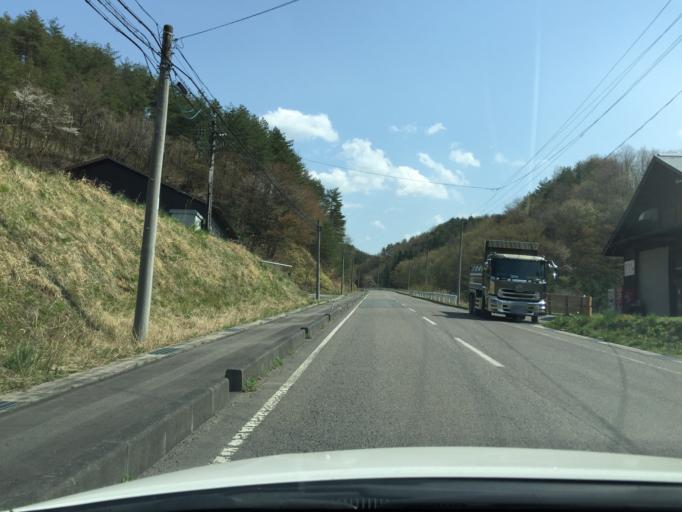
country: JP
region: Fukushima
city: Namie
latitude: 37.4157
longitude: 140.7939
